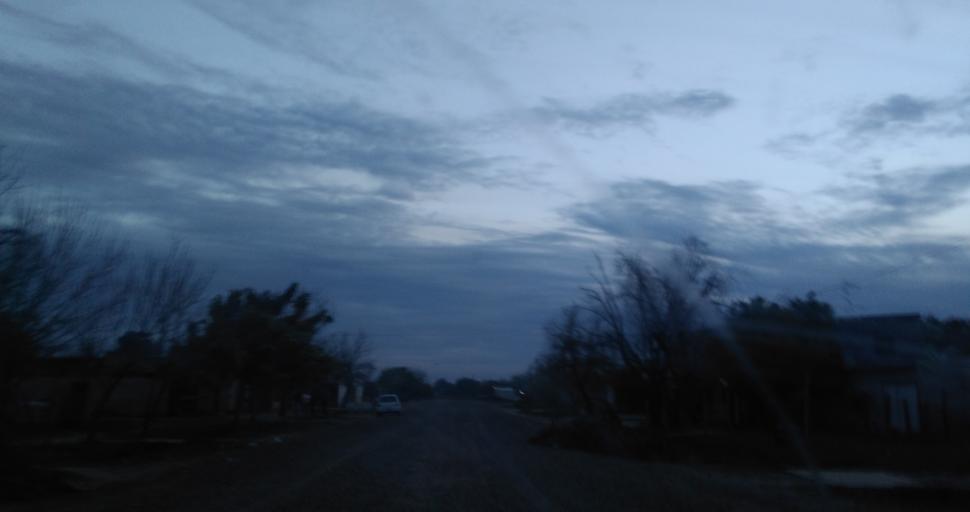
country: AR
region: Chaco
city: Resistencia
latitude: -27.4842
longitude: -59.0037
